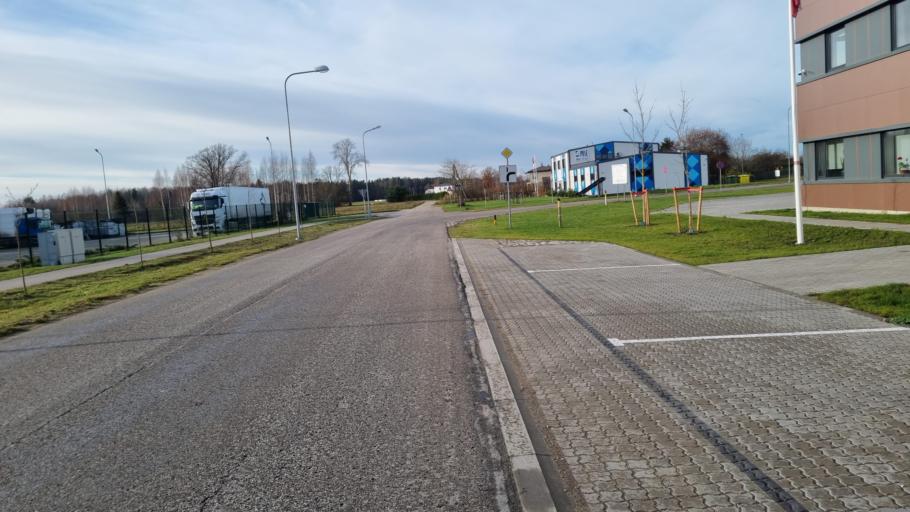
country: LV
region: Marupe
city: Marupe
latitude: 56.9106
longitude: 23.9991
